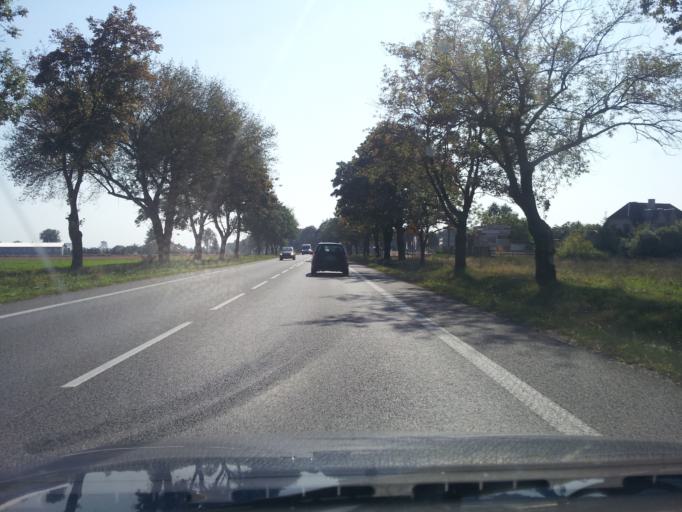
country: PL
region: Masovian Voivodeship
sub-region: Powiat sierpecki
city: Sierpc
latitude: 52.8470
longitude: 19.7118
